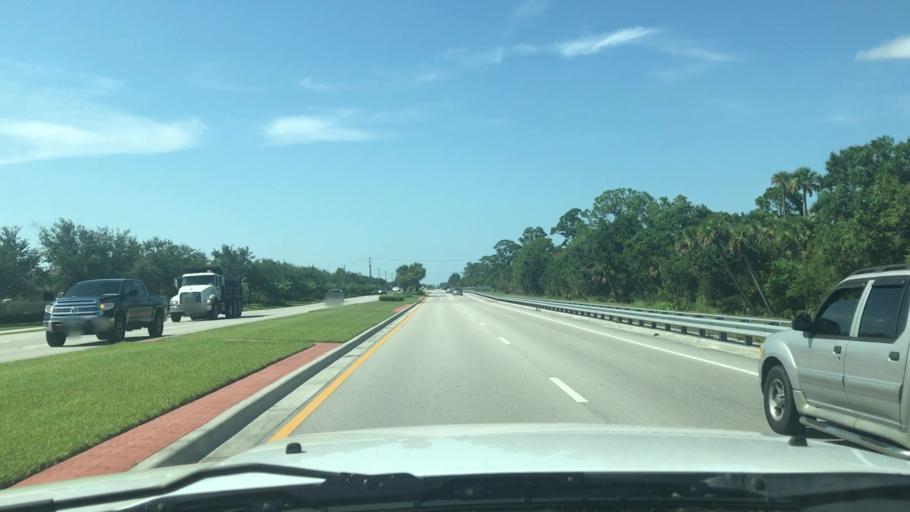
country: US
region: Florida
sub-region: Indian River County
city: West Vero Corridor
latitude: 27.6499
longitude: -80.4631
